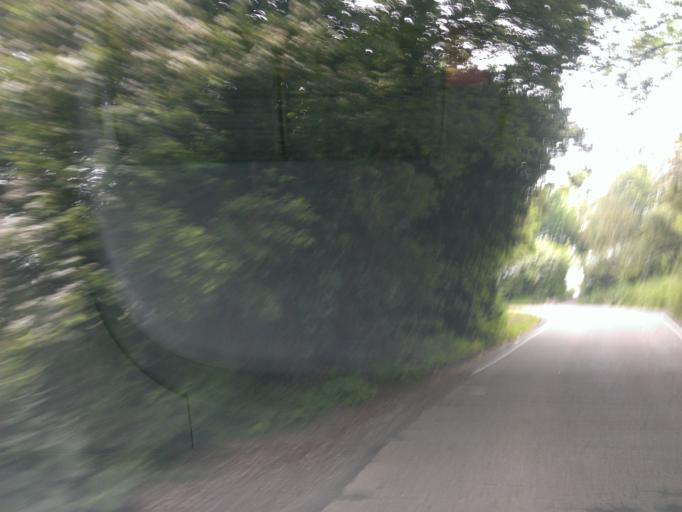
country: GB
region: England
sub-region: Essex
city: West Bergholt
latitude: 51.8986
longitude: 0.8648
